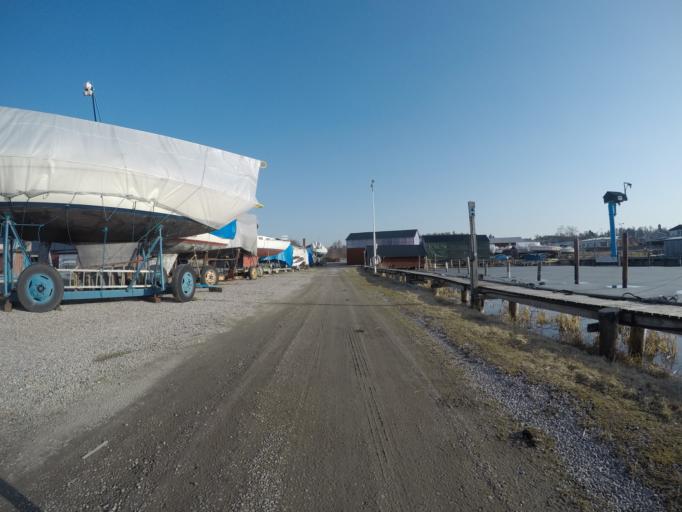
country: SE
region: Vaestmanland
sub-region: Kungsors Kommun
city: Kungsoer
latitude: 59.4302
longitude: 16.1051
